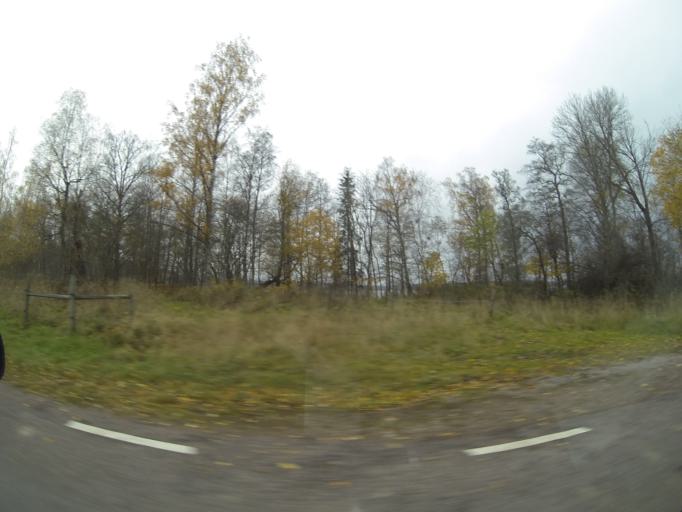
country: SE
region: Vaestmanland
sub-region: Surahammars Kommun
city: Surahammar
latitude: 59.6797
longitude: 16.0814
